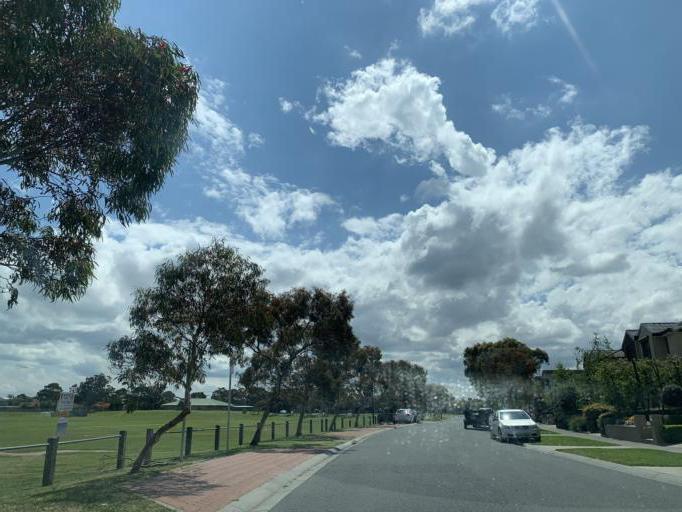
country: AU
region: Victoria
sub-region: Kingston
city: Mordialloc
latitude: -38.0059
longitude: 145.0993
